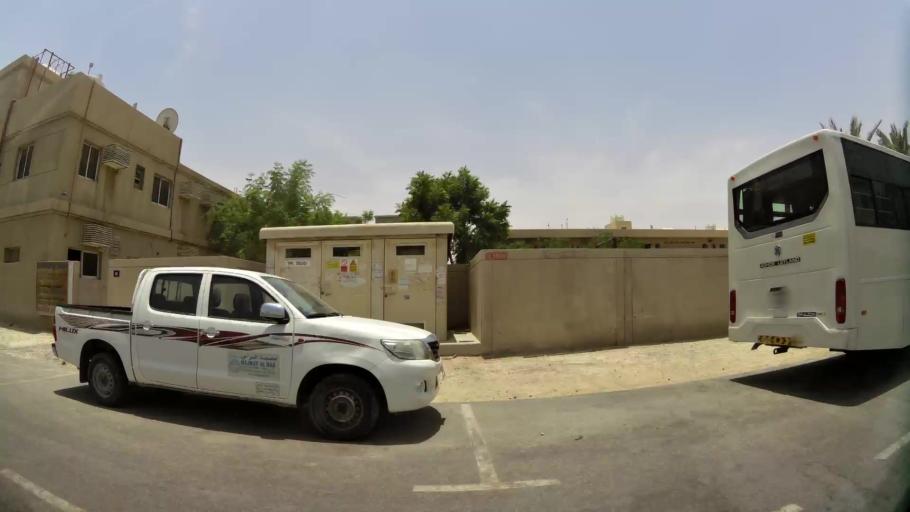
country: AE
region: Ash Shariqah
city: Sharjah
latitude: 25.2680
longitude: 55.4309
